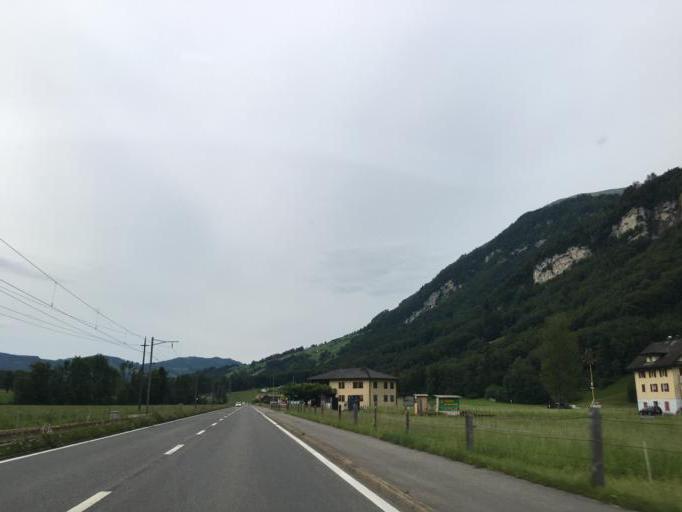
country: CH
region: Nidwalden
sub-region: Nidwalden
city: Dallenwil
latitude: 46.9176
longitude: 8.3967
